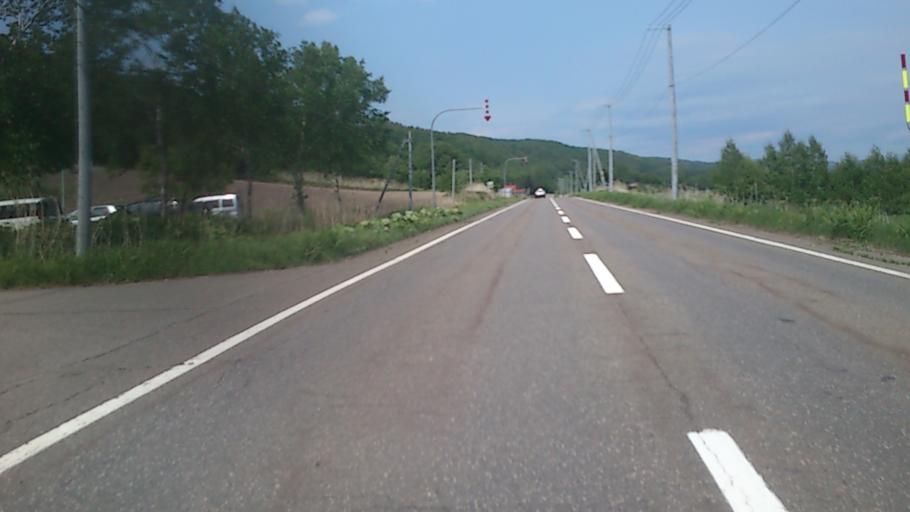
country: JP
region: Hokkaido
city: Otofuke
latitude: 43.2572
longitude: 143.5708
